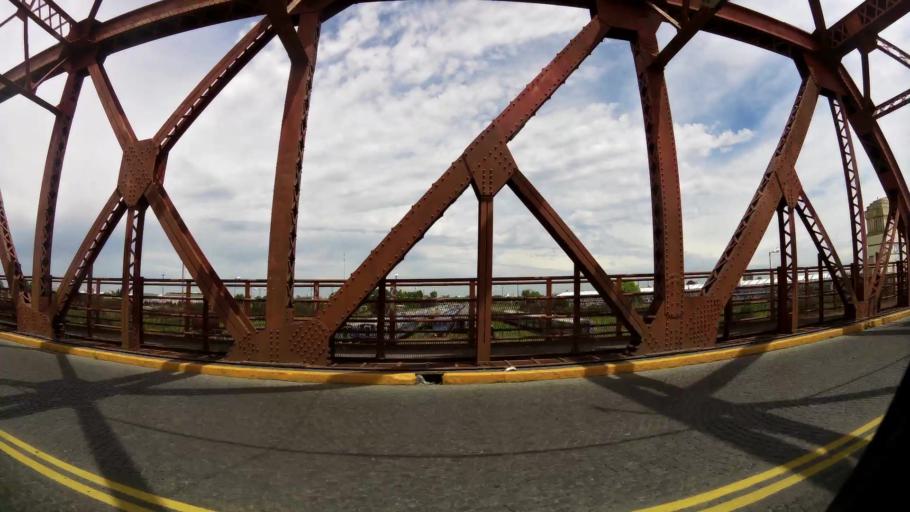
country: AR
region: Buenos Aires
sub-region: Partido de Avellaneda
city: Avellaneda
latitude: -34.6732
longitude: -58.3745
